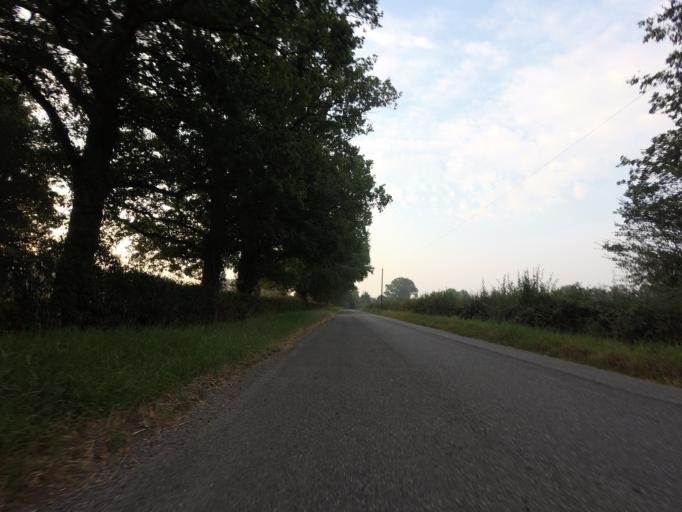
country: GB
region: England
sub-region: Kent
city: Lenham
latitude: 51.1794
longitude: 0.7252
